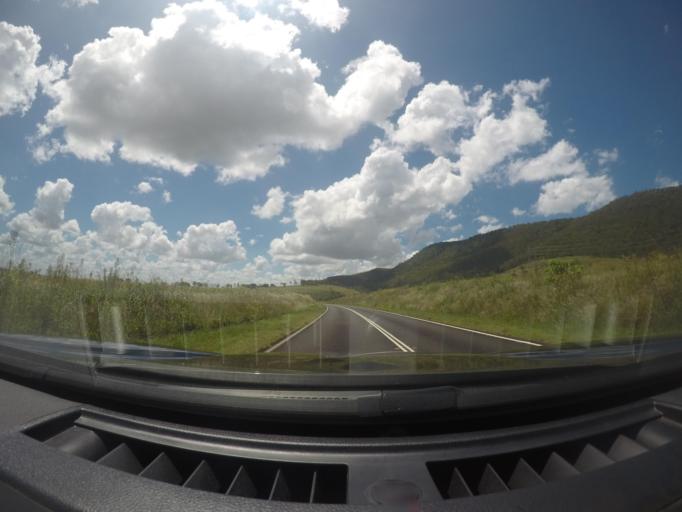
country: AU
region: Queensland
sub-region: Moreton Bay
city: Woodford
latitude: -27.1436
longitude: 152.5239
